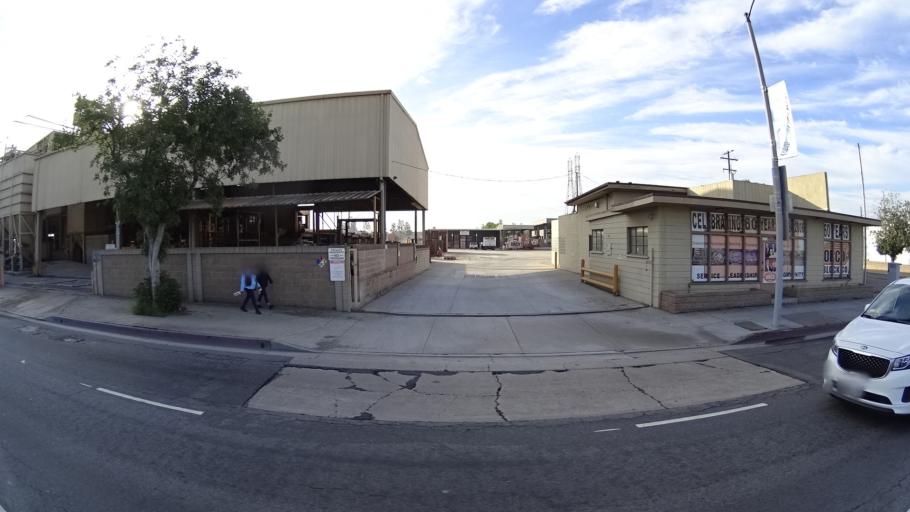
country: US
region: California
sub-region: Orange County
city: Stanton
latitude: 33.8029
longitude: -117.9922
